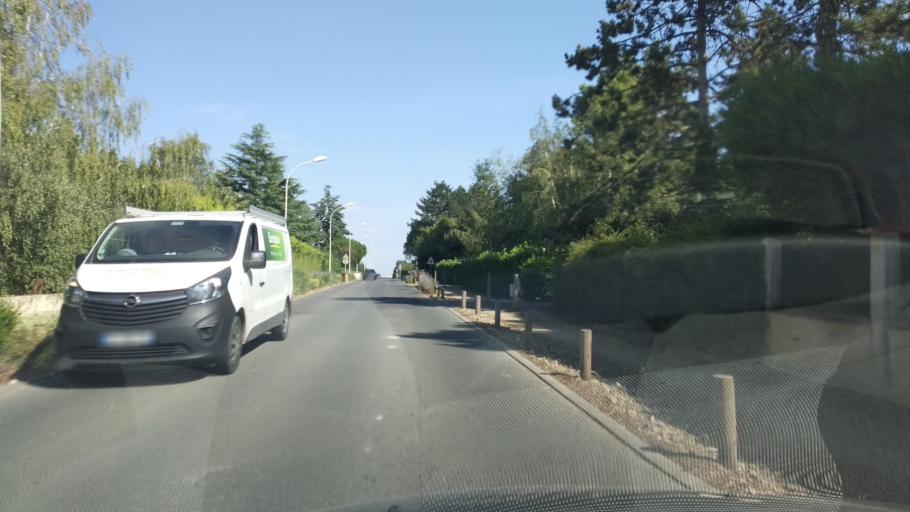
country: FR
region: Poitou-Charentes
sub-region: Departement de la Vienne
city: Cisse
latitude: 46.6375
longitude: 0.2427
